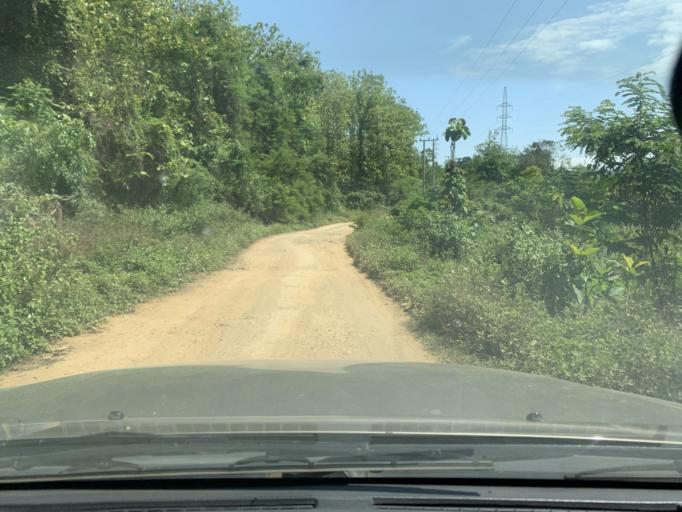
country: LA
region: Louangphabang
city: Louangphabang
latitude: 19.8960
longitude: 102.2092
